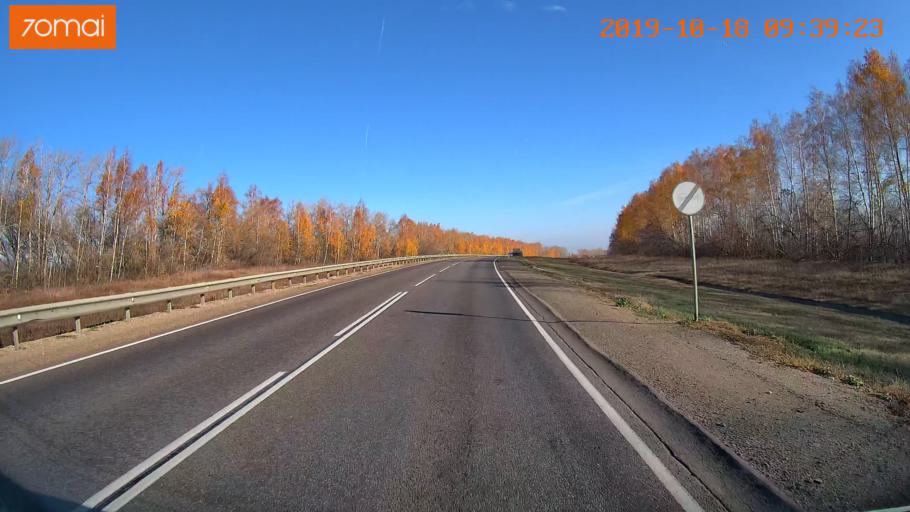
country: RU
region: Tula
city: Yefremov
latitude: 53.2524
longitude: 38.1350
